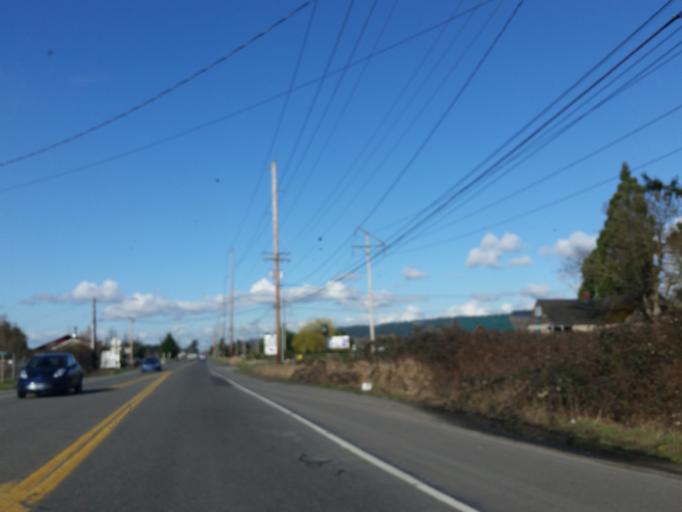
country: US
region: Washington
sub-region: Pierce County
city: Alderton
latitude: 47.1705
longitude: -122.2293
